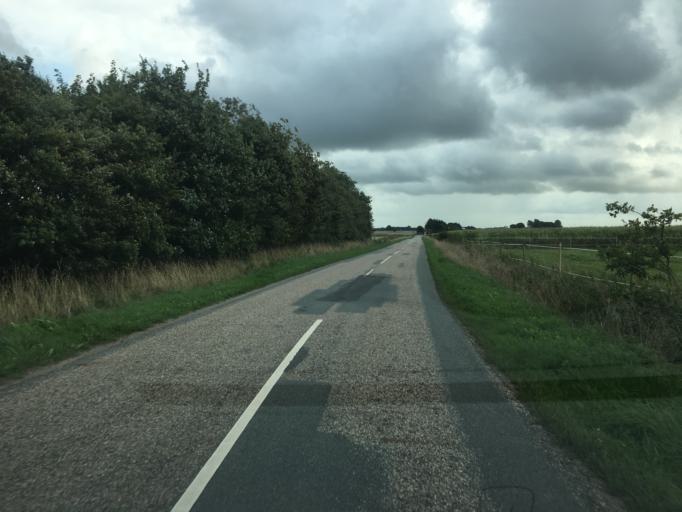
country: DK
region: South Denmark
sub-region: Tonder Kommune
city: Tonder
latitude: 54.9535
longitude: 8.8232
